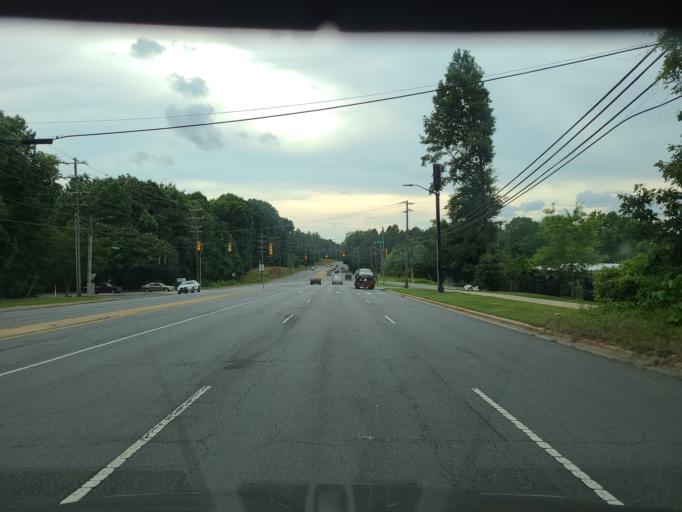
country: US
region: North Carolina
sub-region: Gaston County
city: Belmont
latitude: 35.2355
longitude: -80.9472
